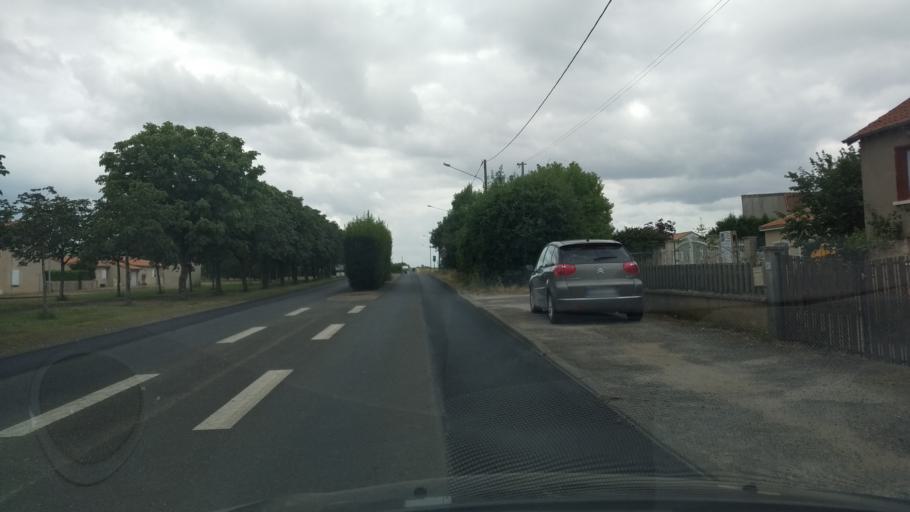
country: FR
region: Poitou-Charentes
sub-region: Departement de la Vienne
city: Roches-Premarie-Andille
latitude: 46.4782
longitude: 0.3693
